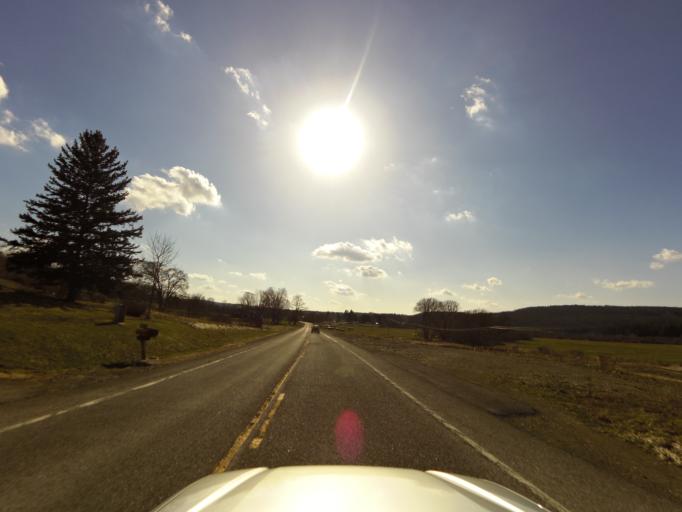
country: US
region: New York
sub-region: Wyoming County
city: Arcade
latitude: 42.4311
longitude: -78.3476
